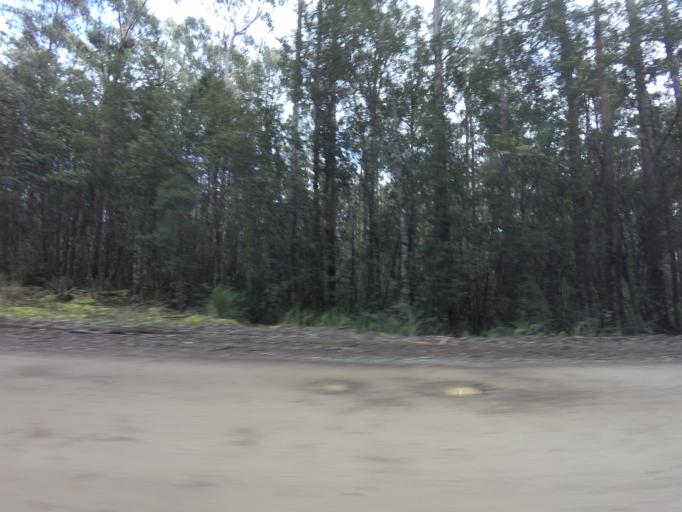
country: AU
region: Tasmania
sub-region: Huon Valley
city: Geeveston
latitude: -43.4933
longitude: 146.8818
